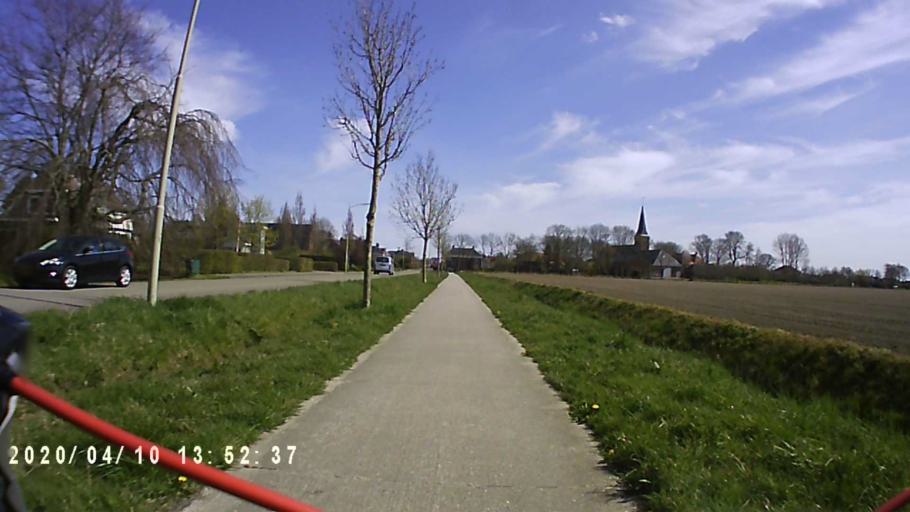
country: NL
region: Groningen
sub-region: Gemeente De Marne
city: Ulrum
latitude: 53.3608
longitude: 6.3691
